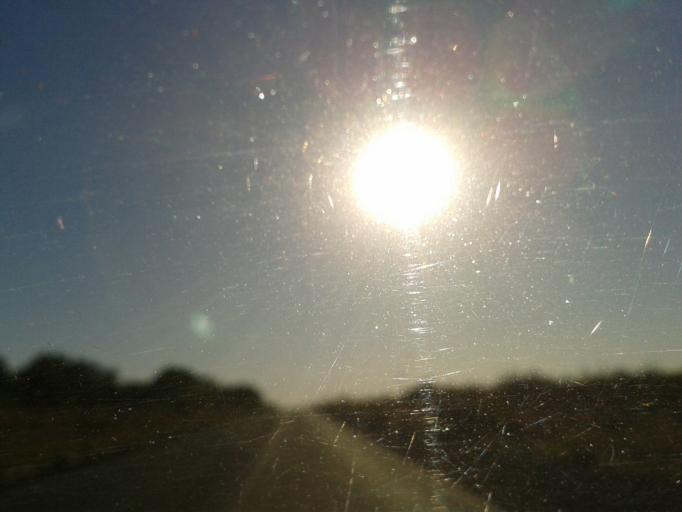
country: BR
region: Minas Gerais
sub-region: Santa Vitoria
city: Santa Vitoria
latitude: -19.1491
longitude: -50.1613
